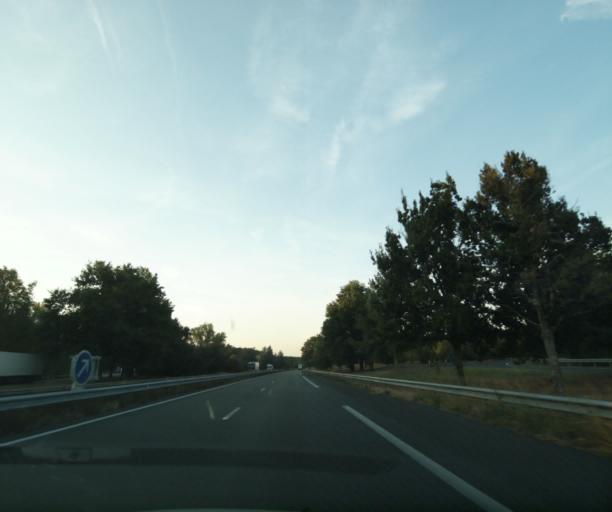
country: FR
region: Aquitaine
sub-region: Departement du Lot-et-Garonne
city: Damazan
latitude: 44.3420
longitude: 0.2516
